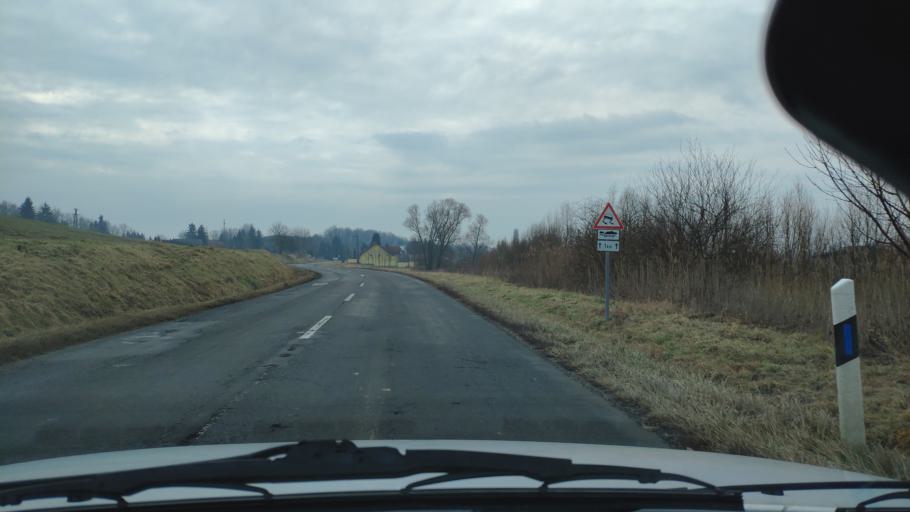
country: HU
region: Zala
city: Nagykanizsa
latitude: 46.5220
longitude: 16.9818
